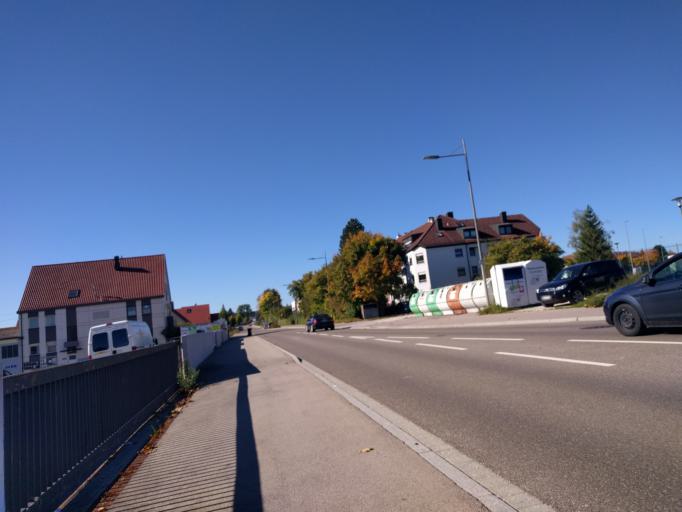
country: DE
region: Bavaria
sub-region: Swabia
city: Donauwoerth
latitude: 48.7182
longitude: 10.7558
